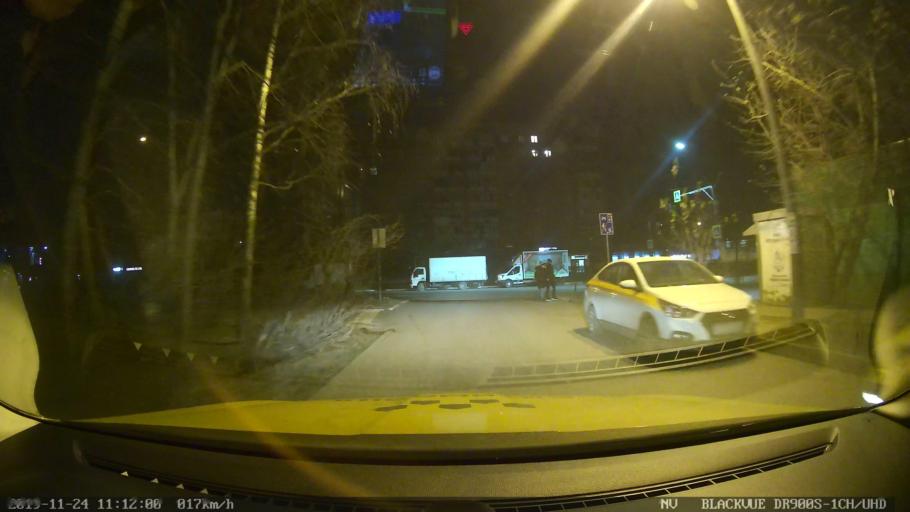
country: RU
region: Moskovskaya
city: Mytishchi
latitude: 55.9038
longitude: 37.7259
